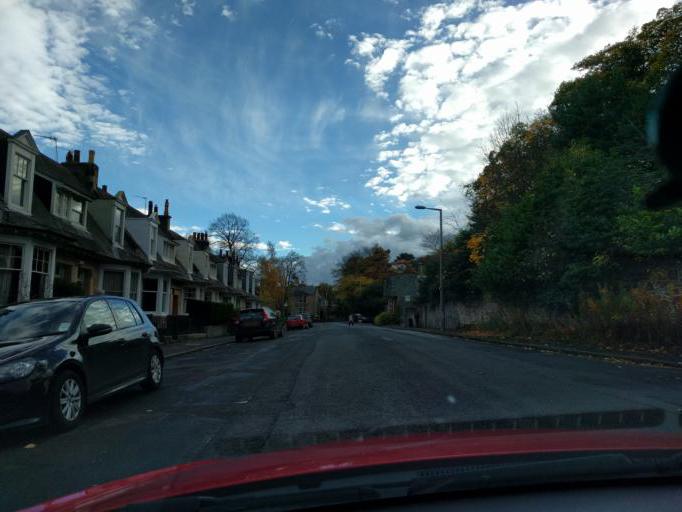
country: GB
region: Scotland
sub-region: Edinburgh
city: Colinton
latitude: 55.9232
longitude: -3.2240
